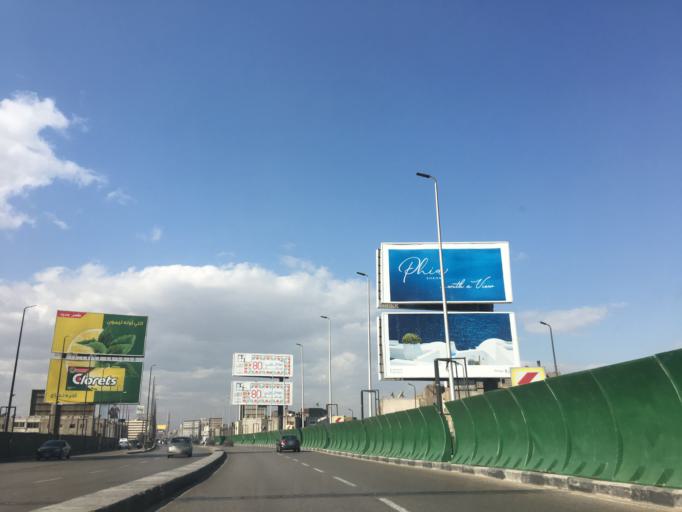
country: EG
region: Muhafazat al Qahirah
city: Cairo
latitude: 30.0618
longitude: 31.3007
